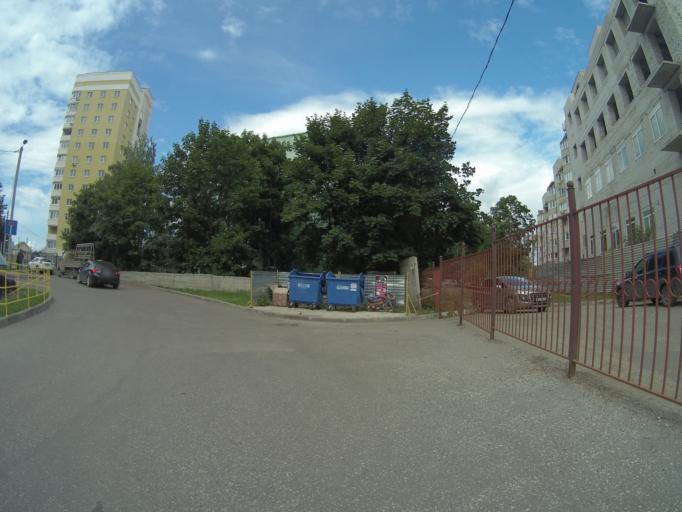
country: RU
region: Vladimir
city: Vladimir
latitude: 56.1236
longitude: 40.3849
